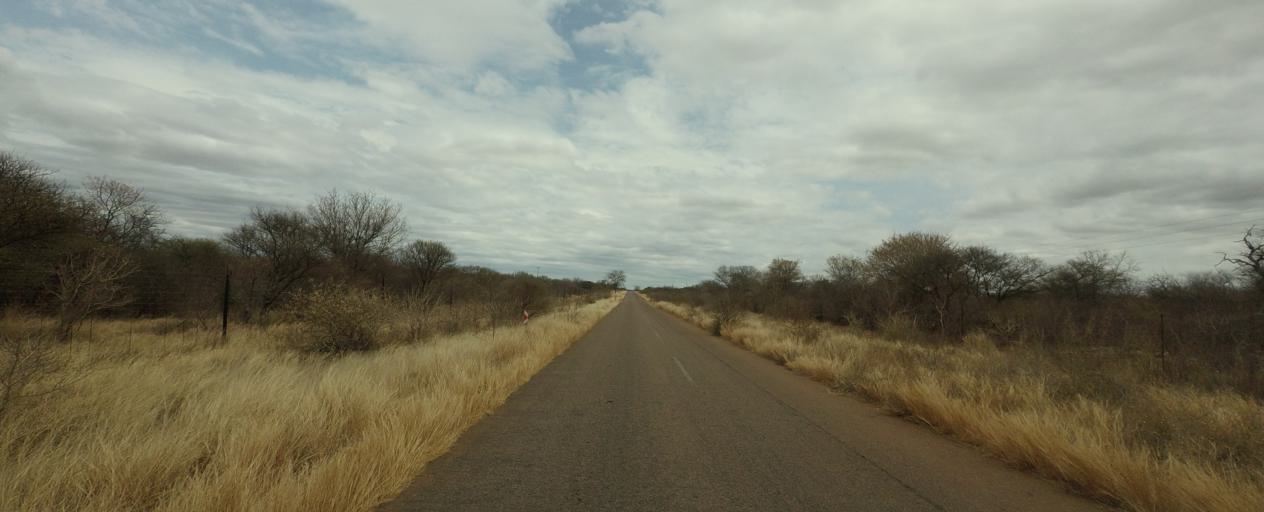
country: BW
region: Central
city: Mathathane
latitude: -22.6634
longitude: 28.7017
